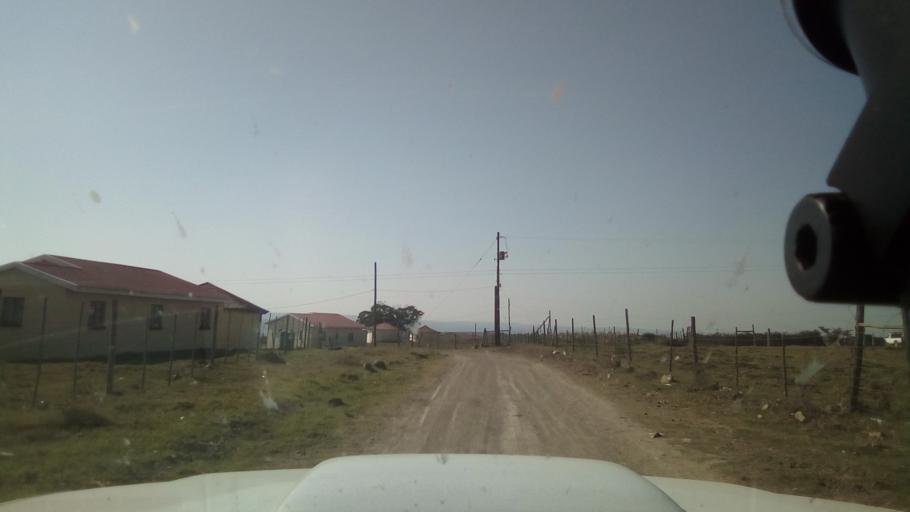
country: ZA
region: Eastern Cape
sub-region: Buffalo City Metropolitan Municipality
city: Bhisho
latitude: -32.9365
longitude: 27.3368
